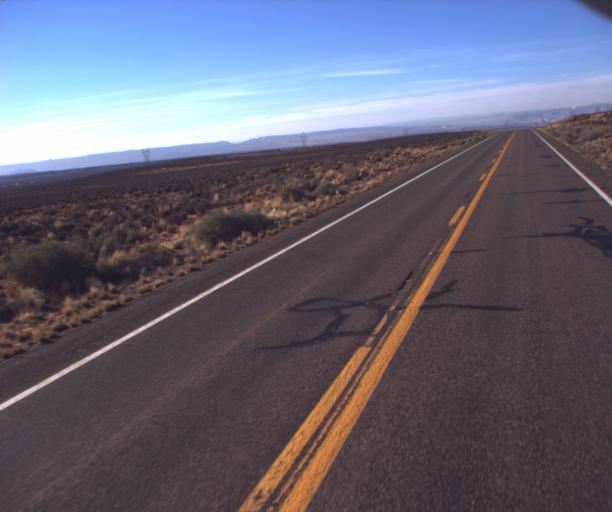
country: US
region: Arizona
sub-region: Coconino County
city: LeChee
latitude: 36.8298
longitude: -111.3124
